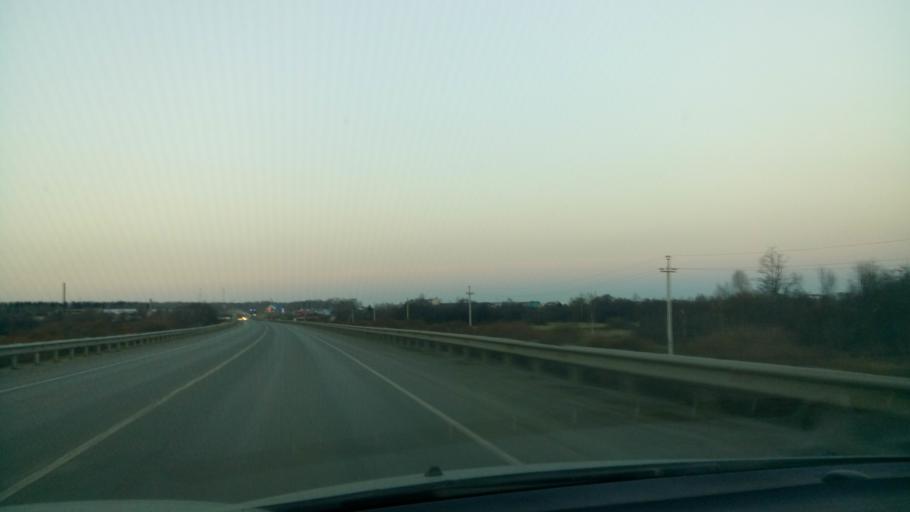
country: RU
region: Sverdlovsk
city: Pyshma
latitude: 56.9433
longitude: 63.2194
